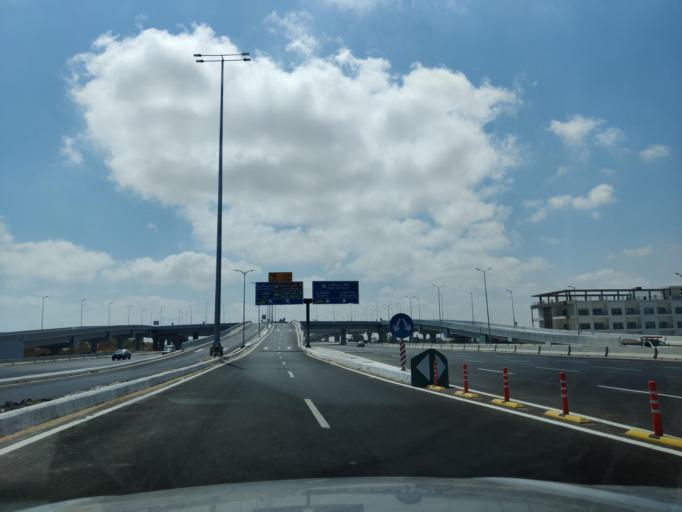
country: EG
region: Muhafazat Matruh
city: Al `Alamayn
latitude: 30.8248
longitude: 28.9829
